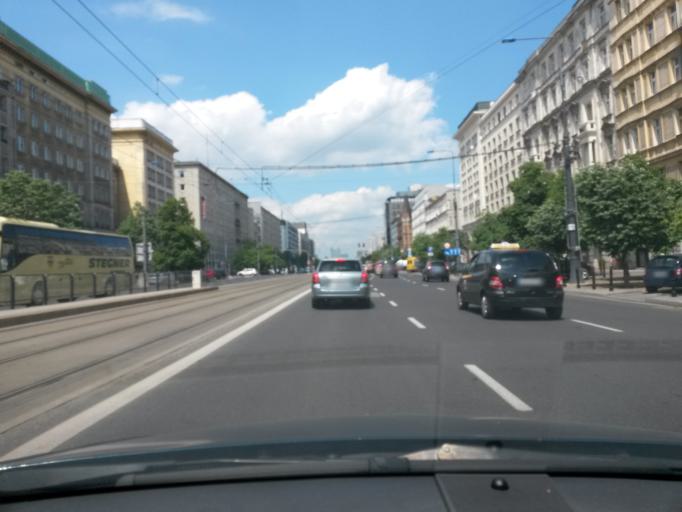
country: PL
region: Masovian Voivodeship
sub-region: Warszawa
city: Srodmiescie
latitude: 52.2237
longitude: 21.0155
